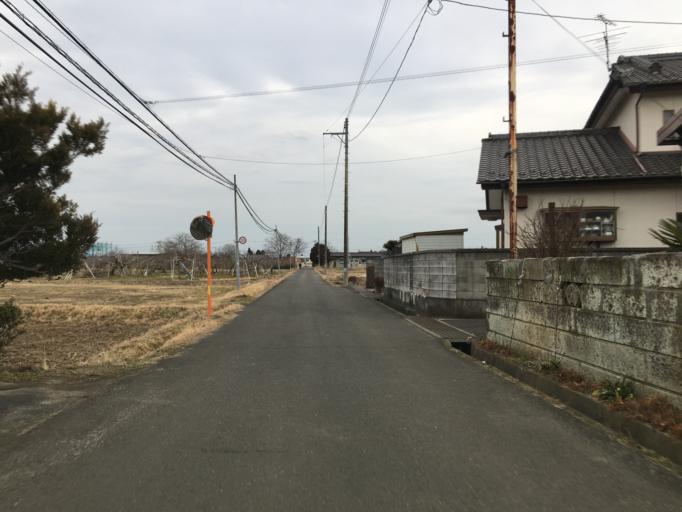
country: JP
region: Fukushima
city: Fukushima-shi
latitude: 37.7469
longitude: 140.4278
